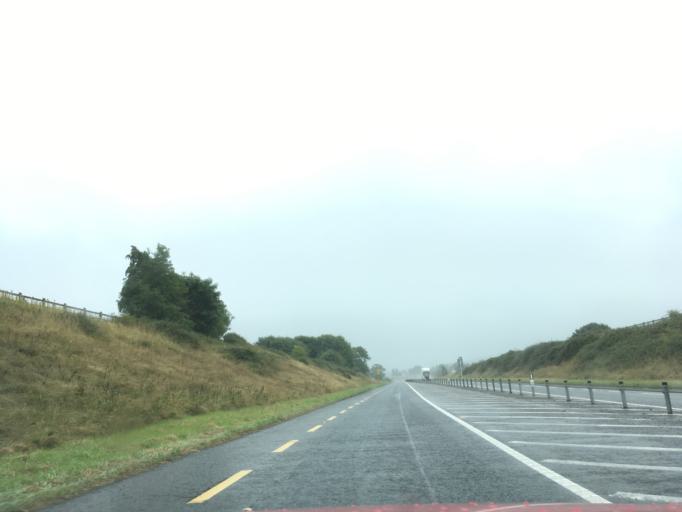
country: IE
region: Leinster
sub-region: Kilkenny
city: Piltown
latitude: 52.3530
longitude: -7.3408
